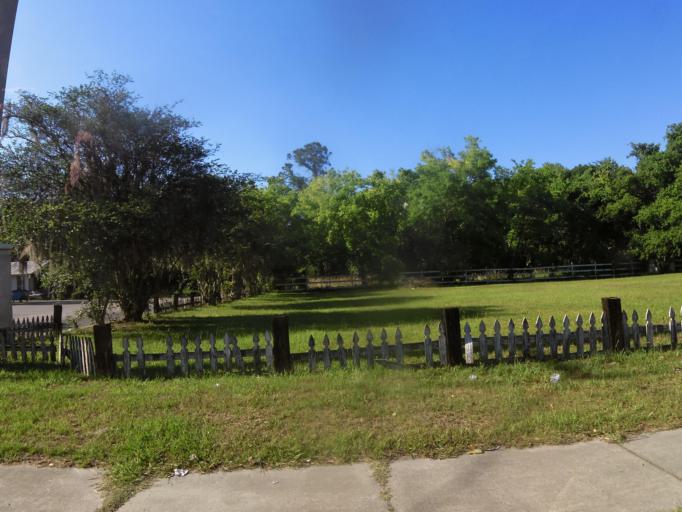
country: US
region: Florida
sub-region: Putnam County
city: Palatka
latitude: 29.6522
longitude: -81.6483
